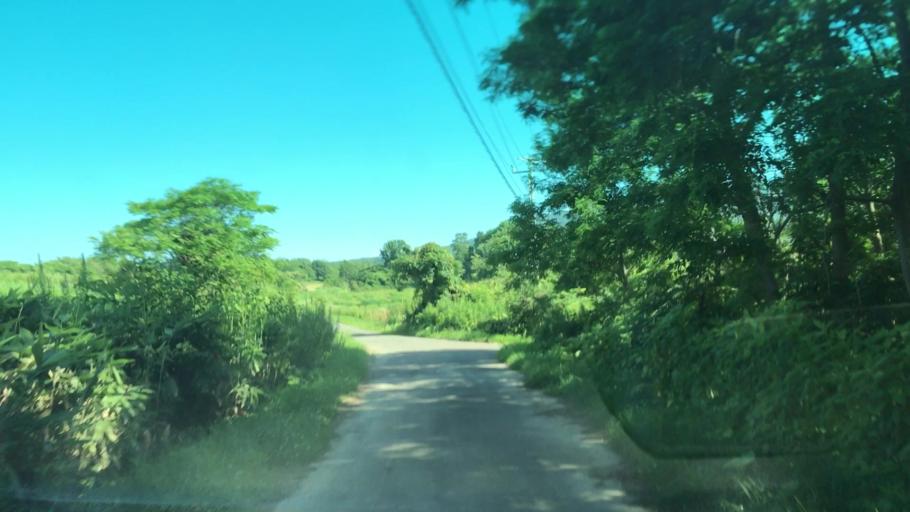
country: JP
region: Hokkaido
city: Iwanai
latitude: 42.9710
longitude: 140.6103
